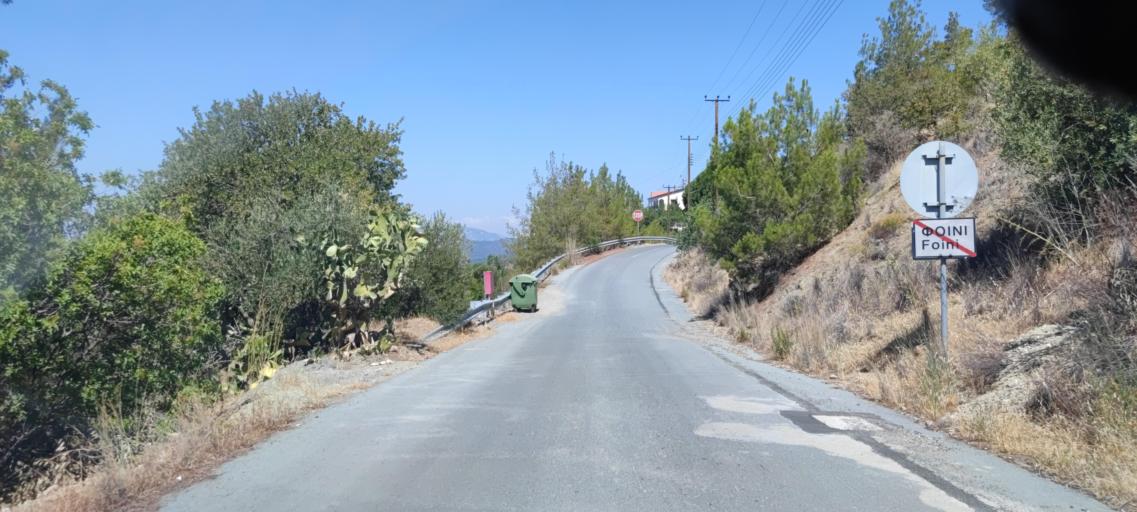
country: CY
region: Lefkosia
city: Kakopetria
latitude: 34.8945
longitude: 32.8311
